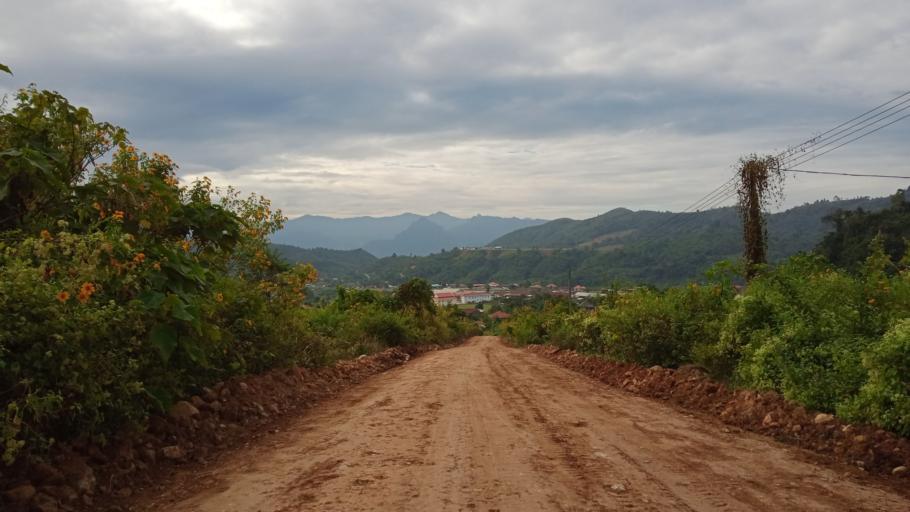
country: LA
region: Xiangkhoang
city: Phonsavan
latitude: 19.1149
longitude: 102.9248
